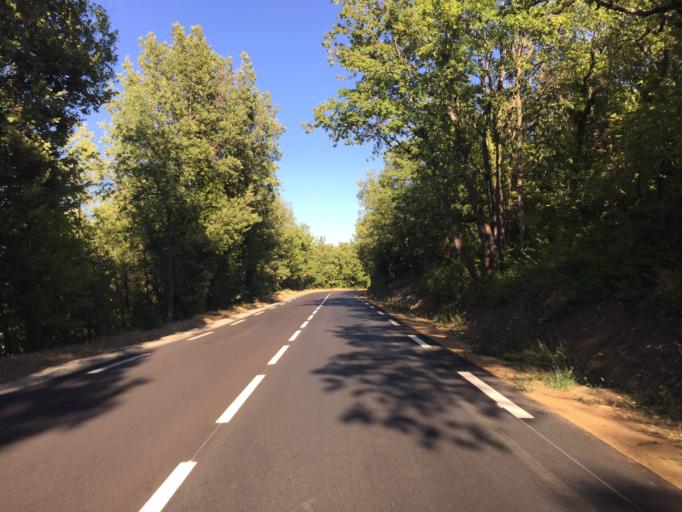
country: FR
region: Provence-Alpes-Cote d'Azur
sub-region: Departement des Alpes-de-Haute-Provence
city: Cereste
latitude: 43.8604
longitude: 5.5737
